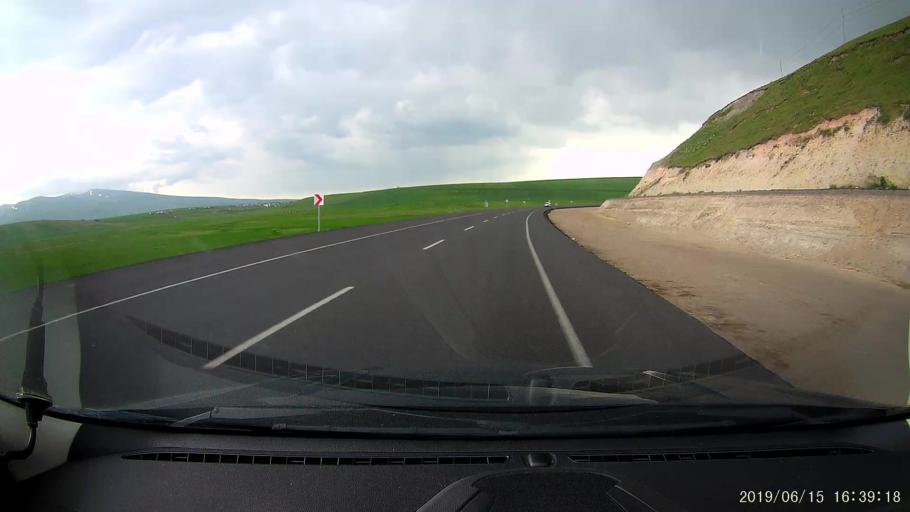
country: TR
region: Ardahan
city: Haskoy
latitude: 40.9843
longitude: 42.8964
